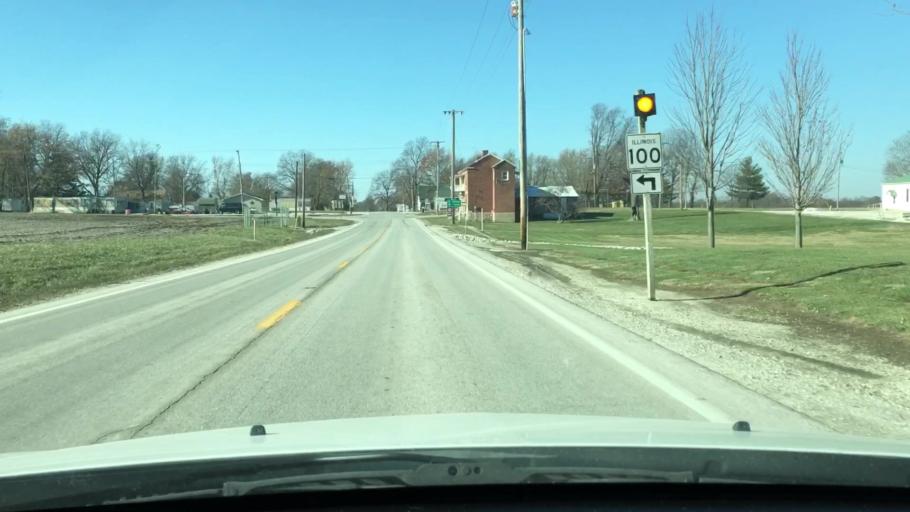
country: US
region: Illinois
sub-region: Pike County
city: Griggsville
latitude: 39.6203
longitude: -90.6742
